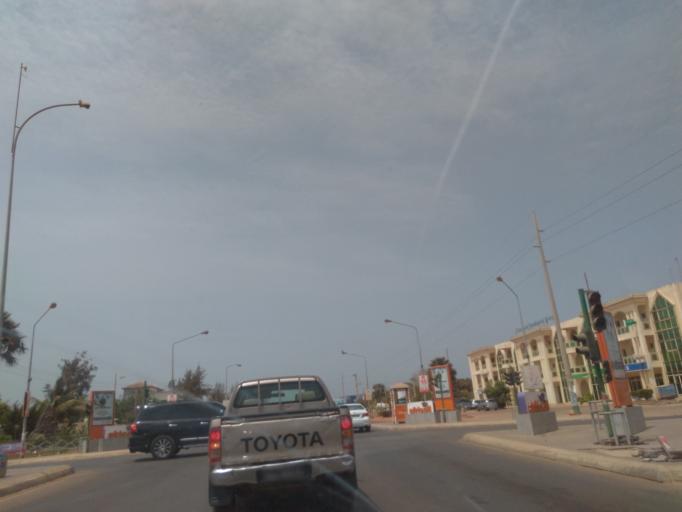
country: GM
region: Banjul
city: Bakau
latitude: 13.4641
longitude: -16.6890
